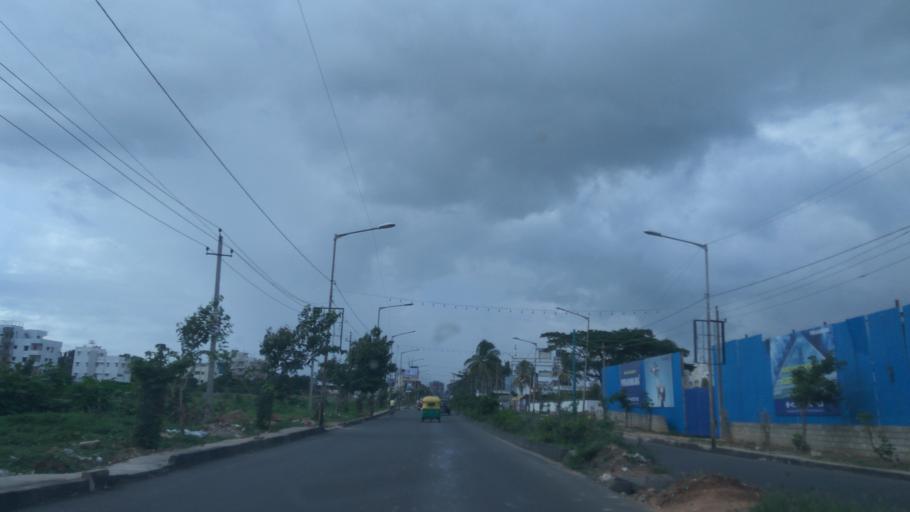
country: IN
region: Karnataka
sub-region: Bangalore Urban
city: Yelahanka
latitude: 13.0639
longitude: 77.6336
